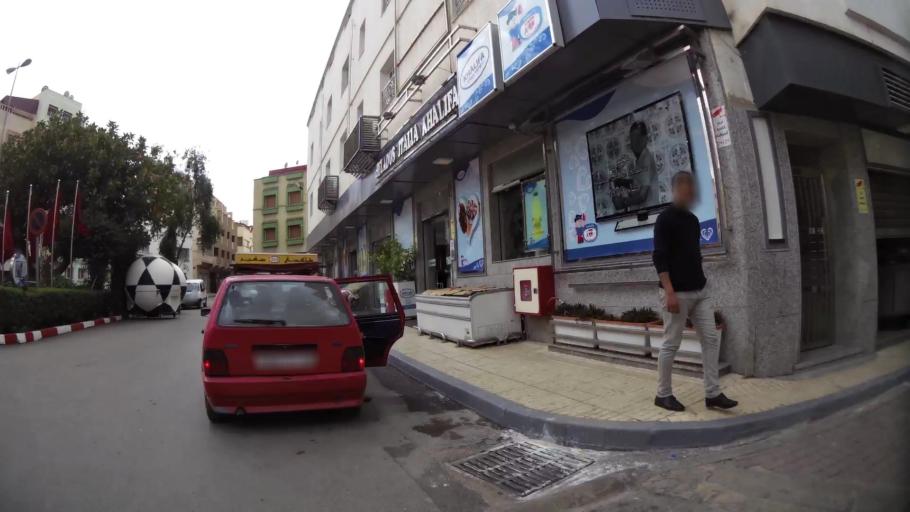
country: MA
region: Oriental
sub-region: Nador
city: Nador
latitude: 35.1736
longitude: -2.9269
